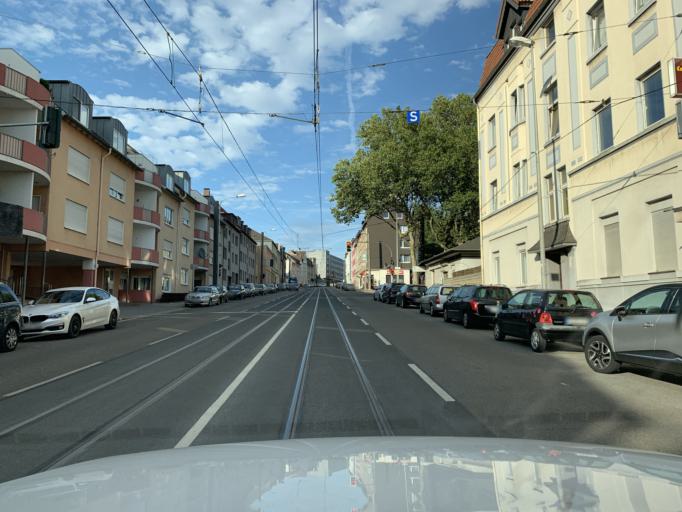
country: DE
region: North Rhine-Westphalia
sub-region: Regierungsbezirk Dusseldorf
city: Muelheim (Ruhr)
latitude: 51.4405
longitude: 6.8947
